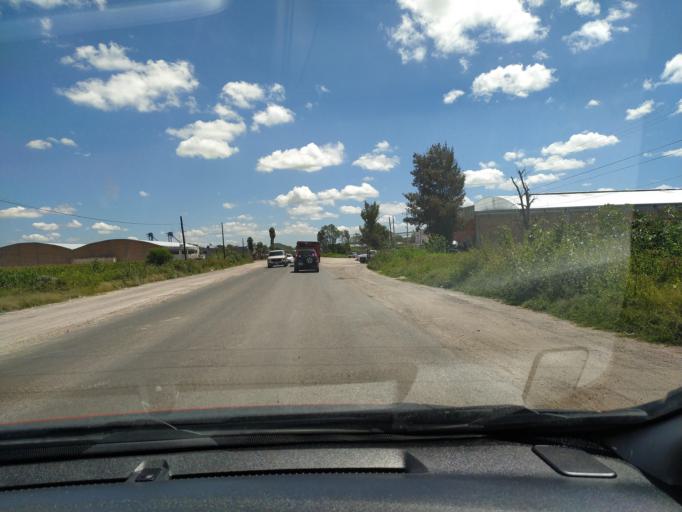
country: MX
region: Jalisco
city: San Julian
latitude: 21.0071
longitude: -102.1615
